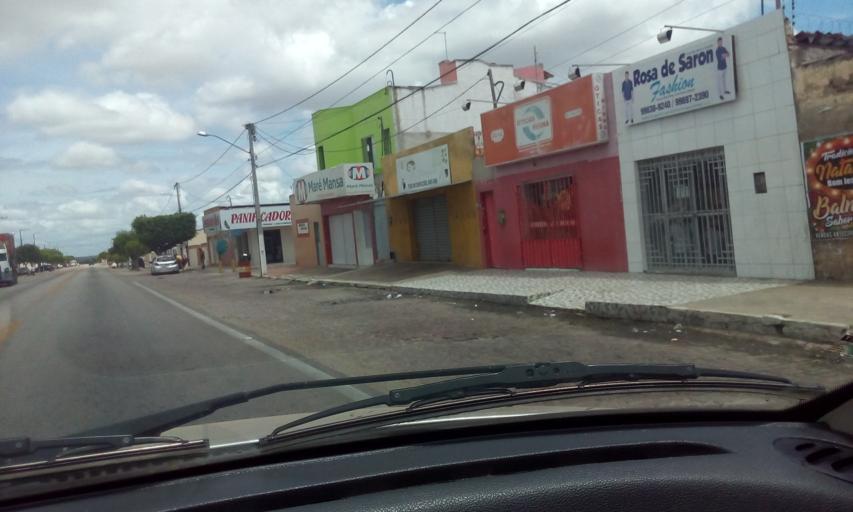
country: BR
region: Rio Grande do Norte
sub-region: Tangara
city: Tangara
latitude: -6.1991
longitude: -35.8004
